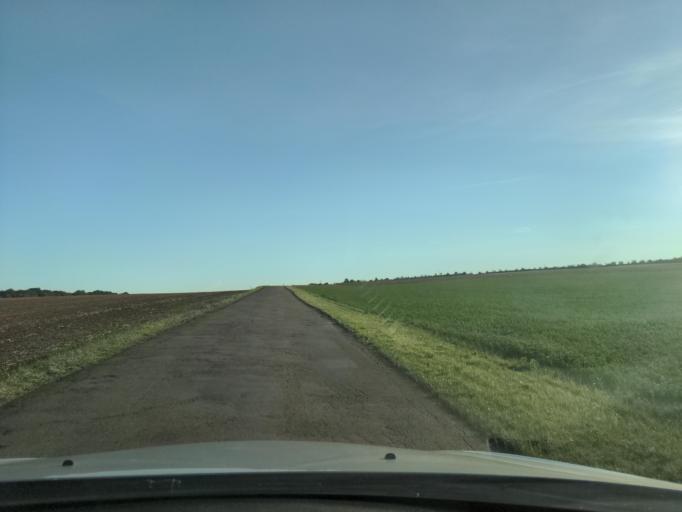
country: FR
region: Bourgogne
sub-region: Departement de la Cote-d'Or
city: Ruffey-les-Echirey
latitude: 47.3944
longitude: 5.0819
